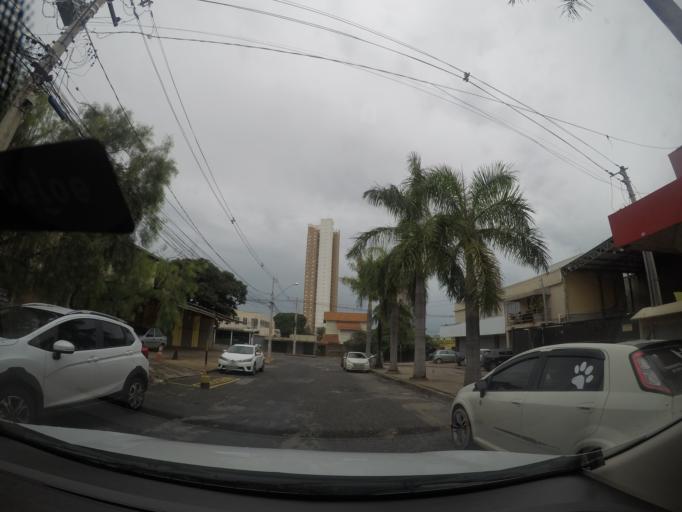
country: BR
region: Goias
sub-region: Goiania
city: Goiania
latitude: -16.6807
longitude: -49.2379
